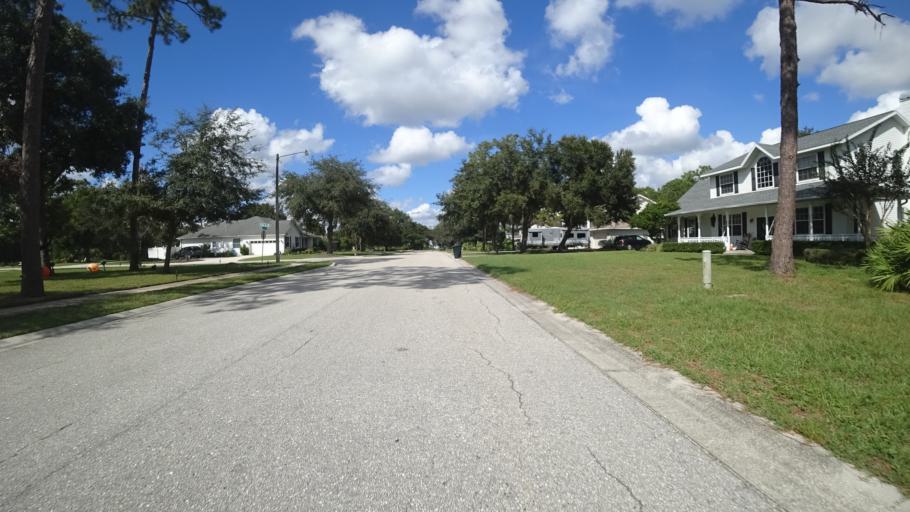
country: US
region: Florida
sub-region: Manatee County
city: Ellenton
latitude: 27.5098
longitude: -82.4013
